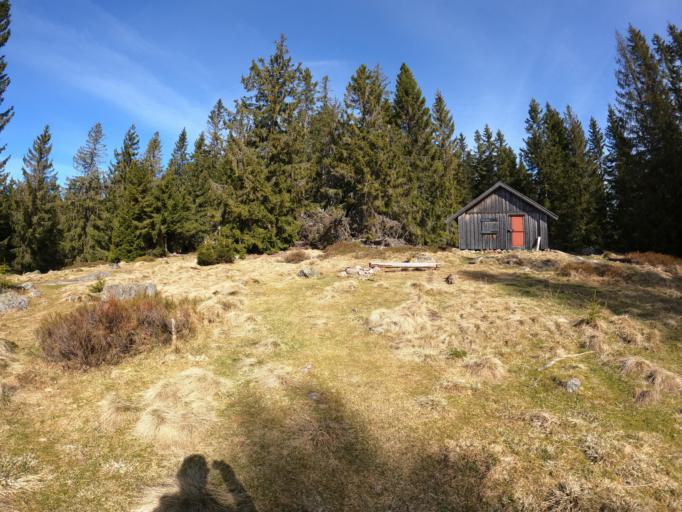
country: NO
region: Akershus
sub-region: Nittedal
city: Aneby
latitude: 60.2010
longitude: 10.8805
